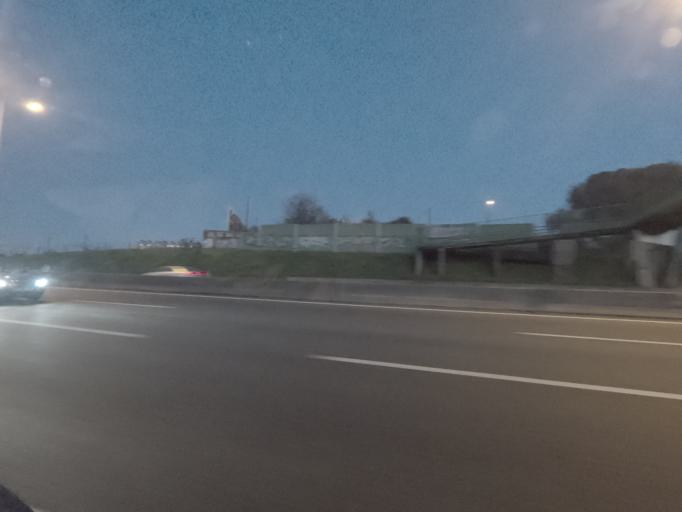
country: PT
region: Porto
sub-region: Maia
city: Pedroucos
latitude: 41.1758
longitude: -8.5946
